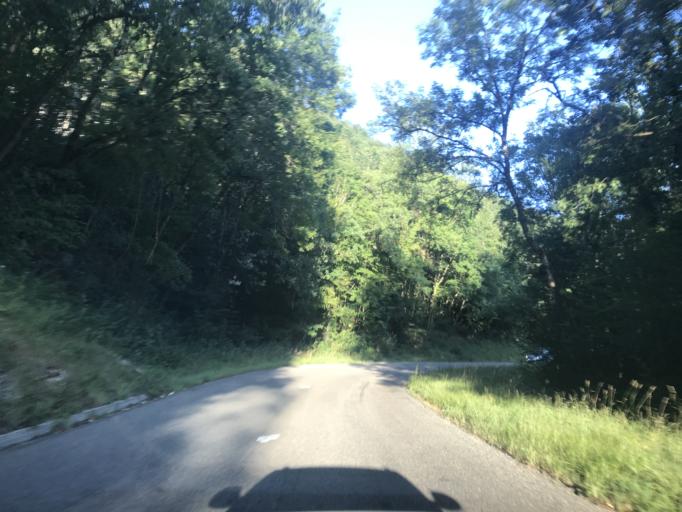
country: FR
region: Rhone-Alpes
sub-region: Departement de la Savoie
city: Brison-Saint-Innocent
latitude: 45.7148
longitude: 5.8255
